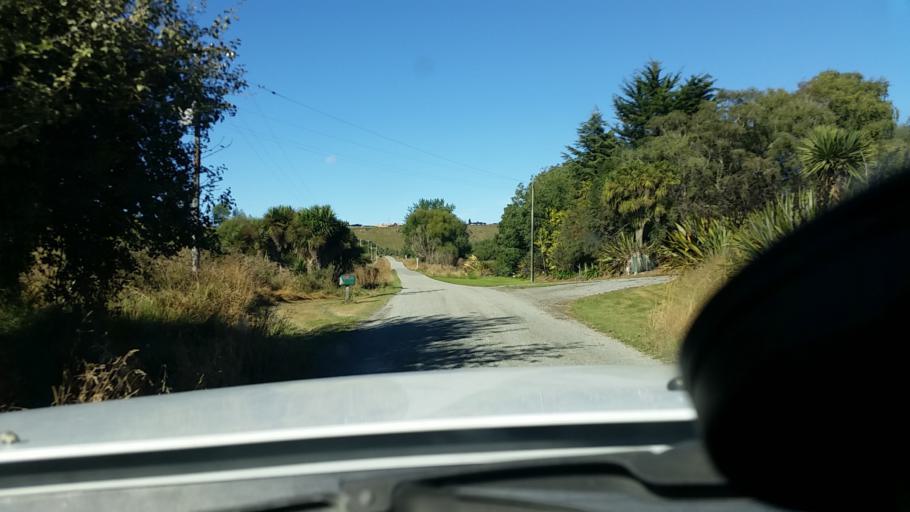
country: NZ
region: Canterbury
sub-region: Timaru District
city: Pleasant Point
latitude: -44.3441
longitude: 171.1596
